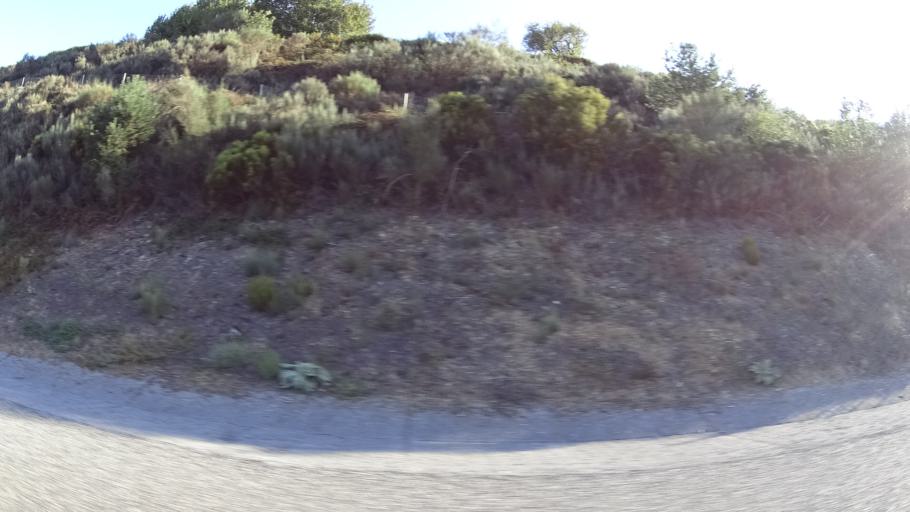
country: ES
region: Galicia
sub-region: Provincia de Lugo
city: San Roman
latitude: 42.7719
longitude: -7.0914
